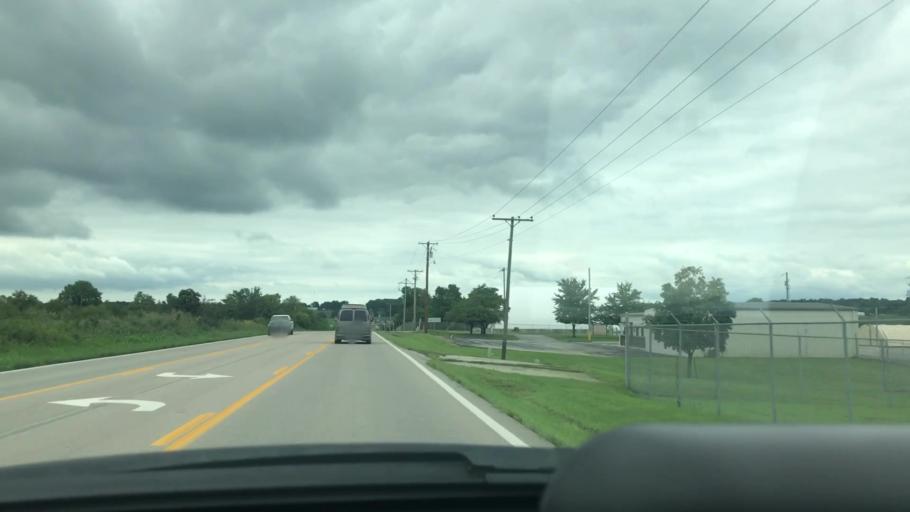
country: US
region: Missouri
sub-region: Dallas County
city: Buffalo
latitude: 37.6592
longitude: -93.1036
